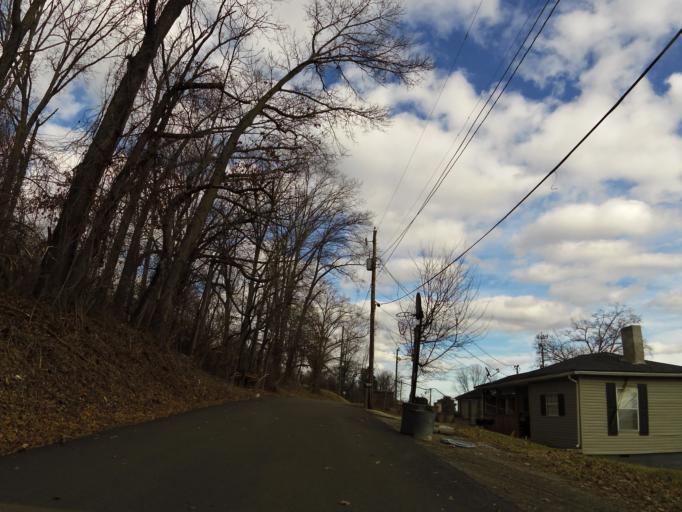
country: US
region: Tennessee
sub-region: Knox County
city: Knoxville
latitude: 35.9886
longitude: -83.9035
